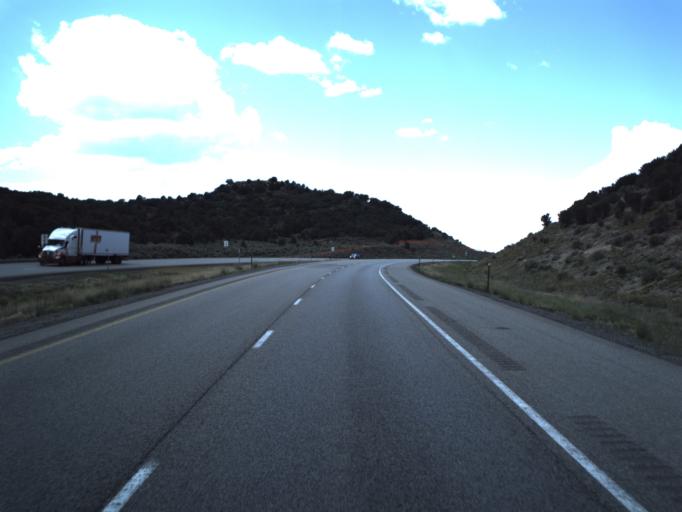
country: US
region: Utah
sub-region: Wayne County
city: Loa
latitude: 38.7784
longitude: -111.4815
